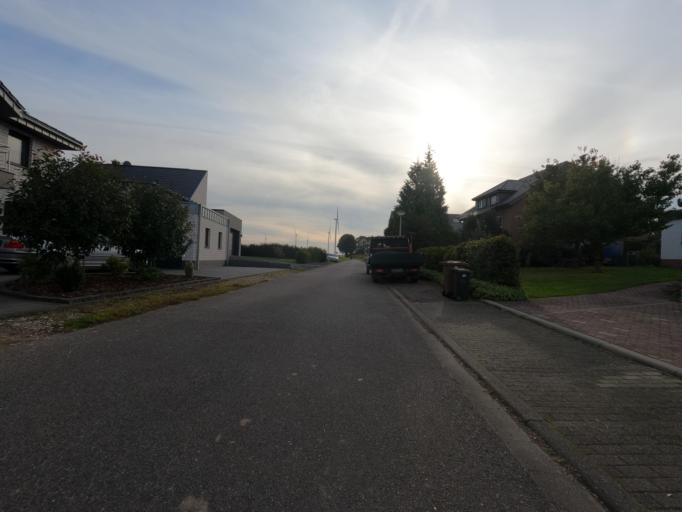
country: DE
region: North Rhine-Westphalia
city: Huckelhoven
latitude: 51.0348
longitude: 6.1698
